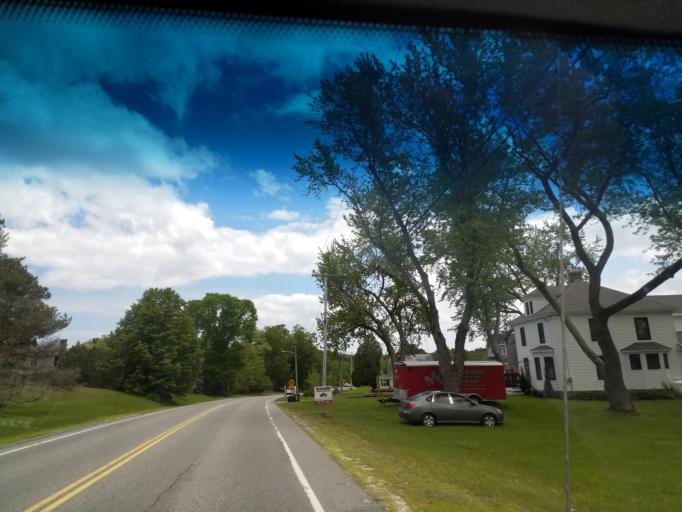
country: US
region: Maine
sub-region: Cumberland County
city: Falmouth
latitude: 43.7420
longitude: -70.2899
